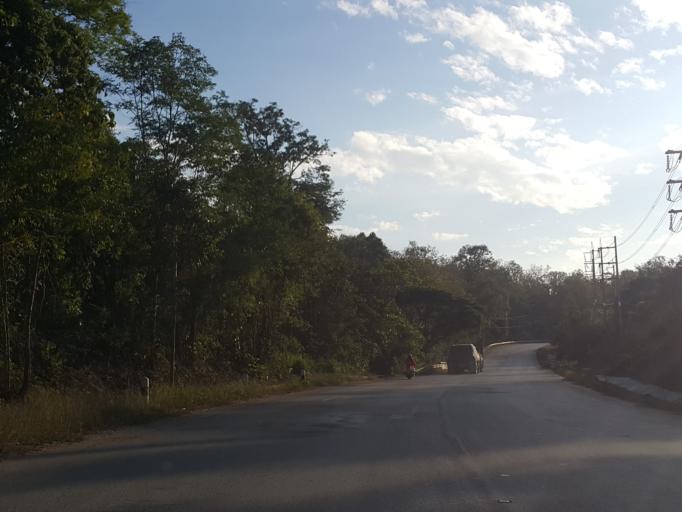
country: TH
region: Lampang
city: Chae Hom
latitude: 18.5355
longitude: 99.5647
